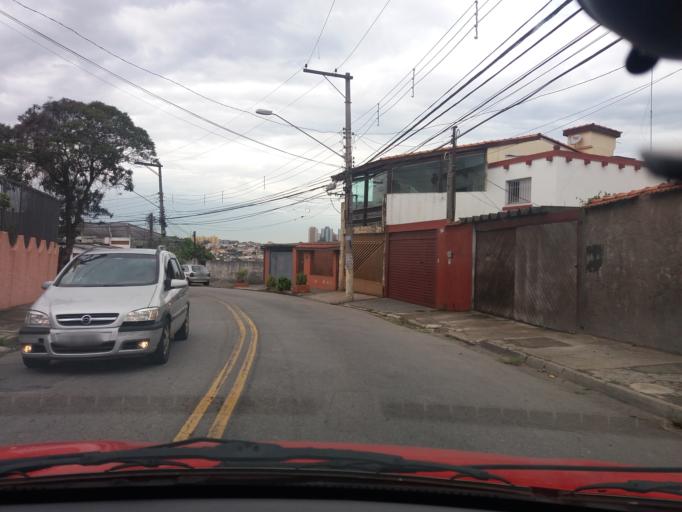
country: BR
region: Sao Paulo
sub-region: Taboao Da Serra
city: Taboao da Serra
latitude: -23.5835
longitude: -46.7399
